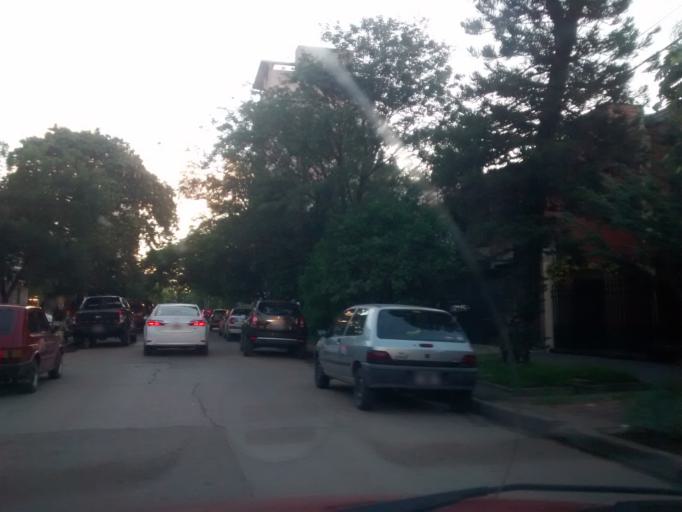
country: AR
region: Chaco
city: Resistencia
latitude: -27.4476
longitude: -58.9790
